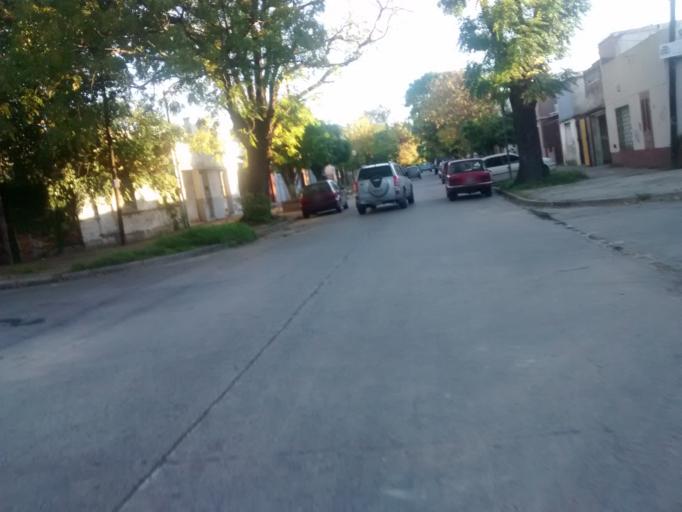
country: AR
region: Buenos Aires
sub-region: Partido de La Plata
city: La Plata
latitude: -34.9139
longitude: -57.9257
